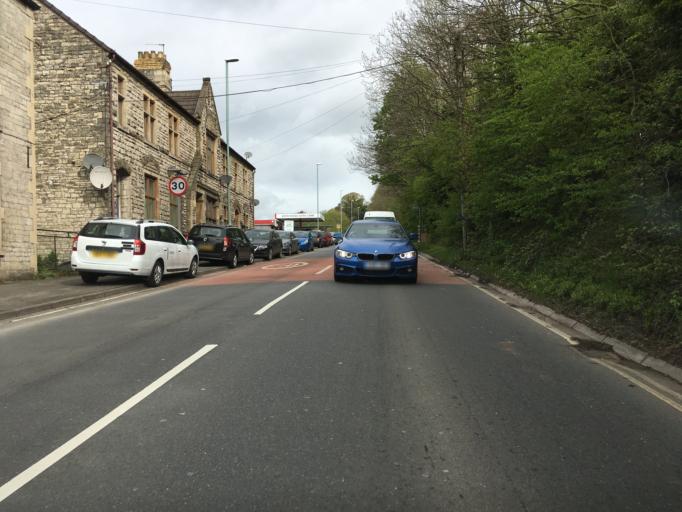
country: GB
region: England
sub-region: Bath and North East Somerset
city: Radstock
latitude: 51.2937
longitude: -2.4482
